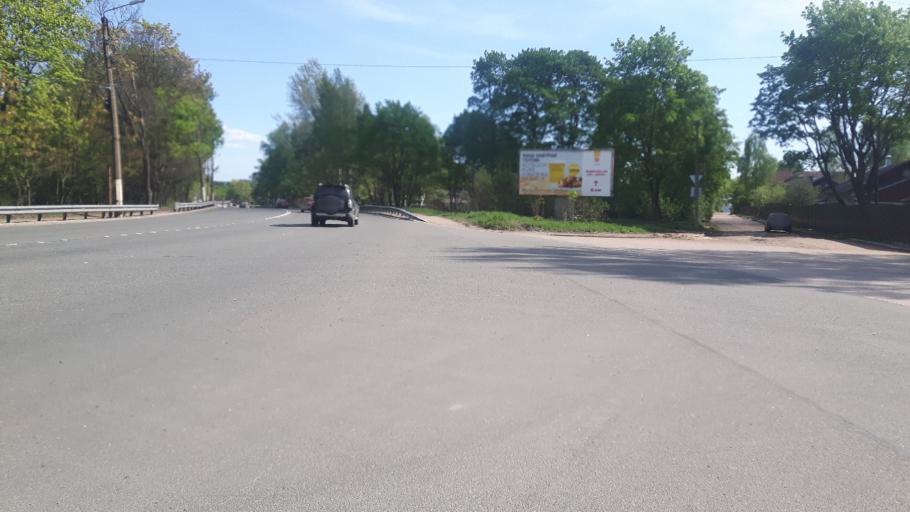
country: RU
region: Leningrad
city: Vyborg
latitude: 60.7301
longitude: 28.6990
